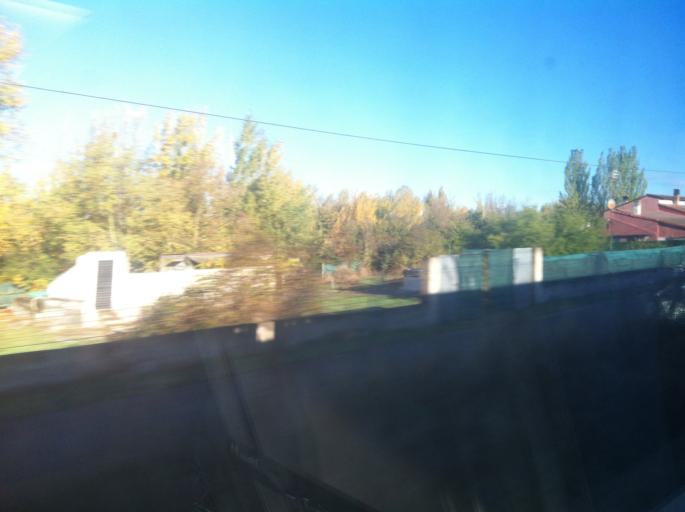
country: ES
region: Castille and Leon
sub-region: Provincia de Valladolid
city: Cubillas de Santa Marta
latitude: 41.8075
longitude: -4.5804
